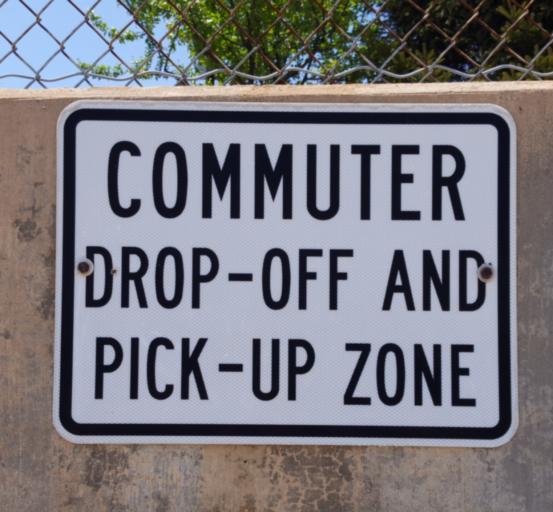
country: US
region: Illinois
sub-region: Lake County
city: Deerfield
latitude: 42.1678
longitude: -87.8495
